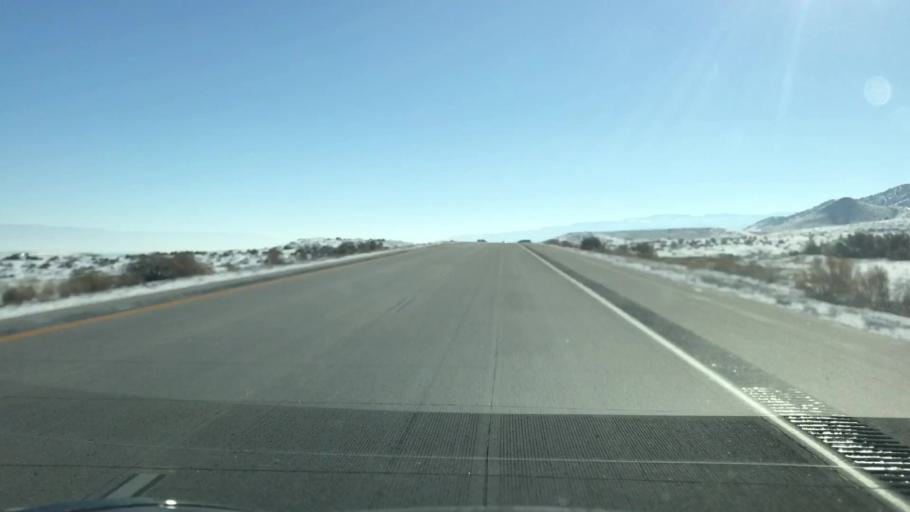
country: US
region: Colorado
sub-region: Mesa County
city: Loma
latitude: 39.1966
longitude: -108.8476
